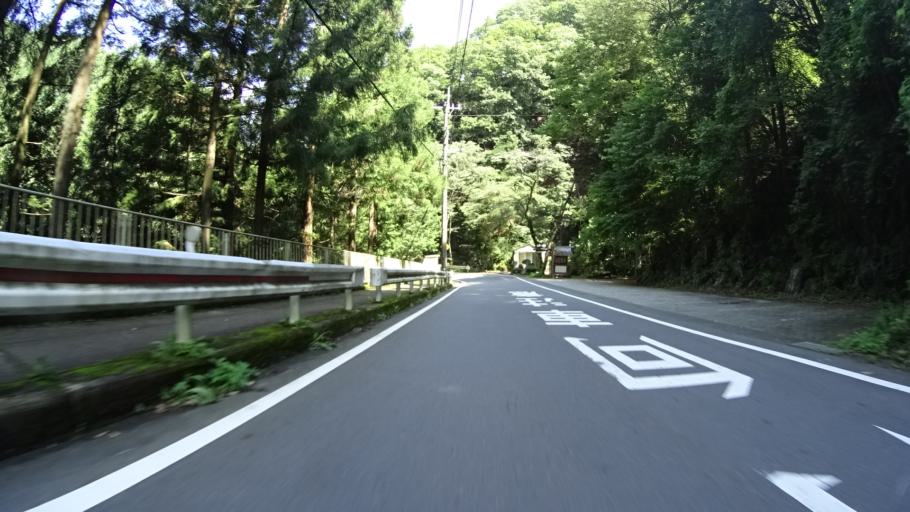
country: JP
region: Gunma
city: Tomioka
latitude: 36.0717
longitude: 138.8298
